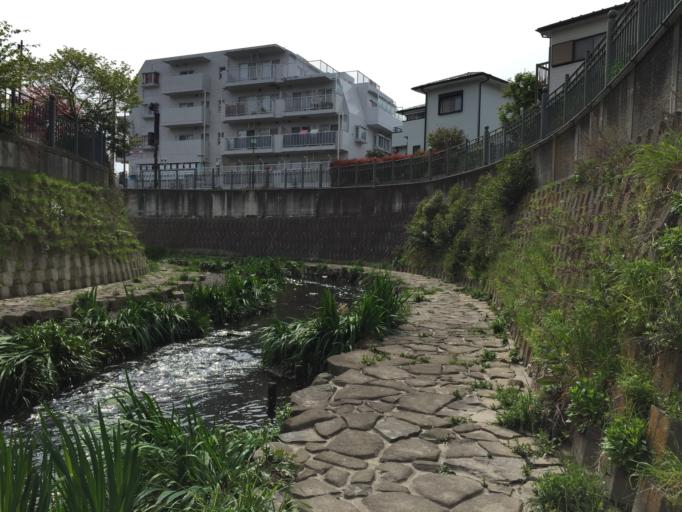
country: JP
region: Kanagawa
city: Yokohama
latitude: 35.4112
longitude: 139.5958
